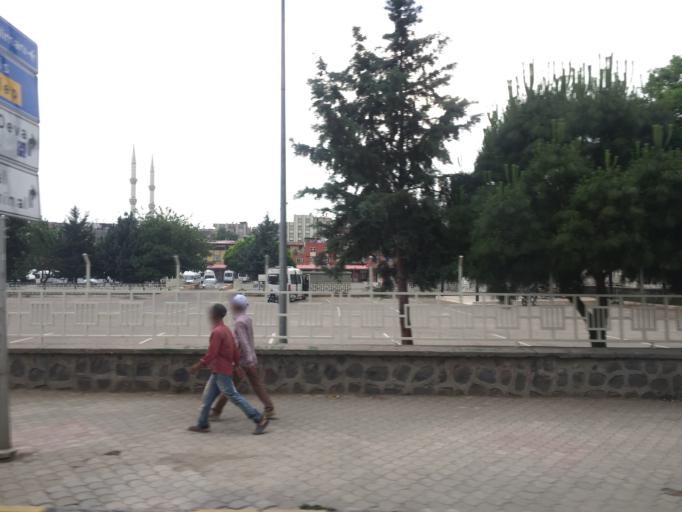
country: TR
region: Gaziantep
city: Gaziantep
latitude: 37.0682
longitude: 37.4141
